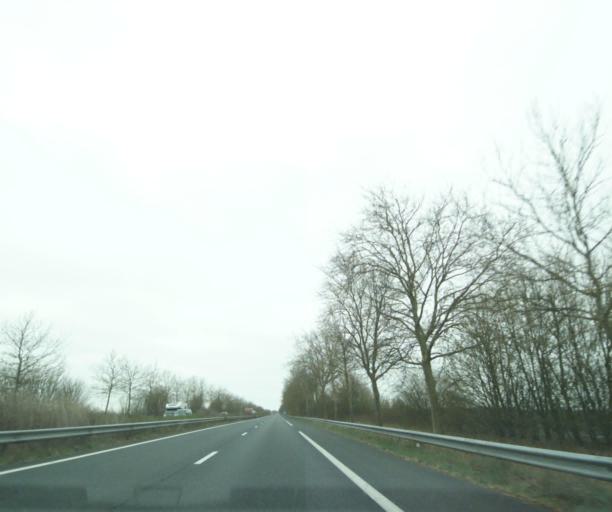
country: FR
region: Centre
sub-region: Departement de l'Indre
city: Montierchaume
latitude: 46.9006
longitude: 1.7330
